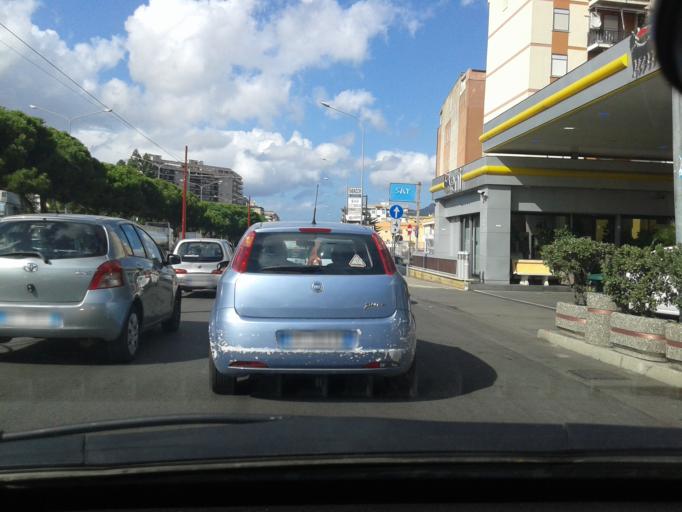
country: IT
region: Sicily
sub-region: Palermo
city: Palermo
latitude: 38.1196
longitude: 13.3290
